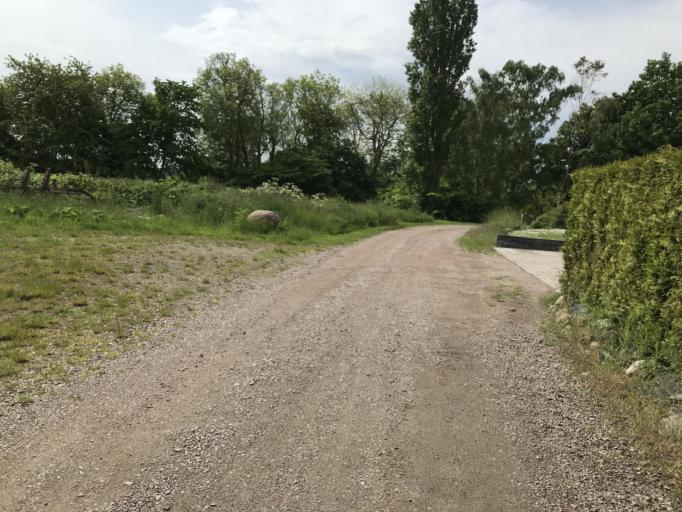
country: SE
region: Skane
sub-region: Landskrona
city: Landskrona
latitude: 55.9050
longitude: 12.8504
